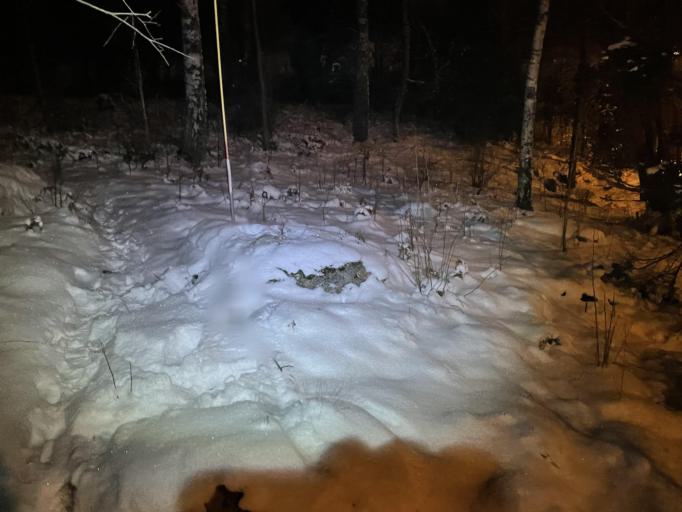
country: SE
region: Joenkoeping
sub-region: Eksjo Kommun
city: Eksjoe
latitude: 57.6519
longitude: 14.9964
